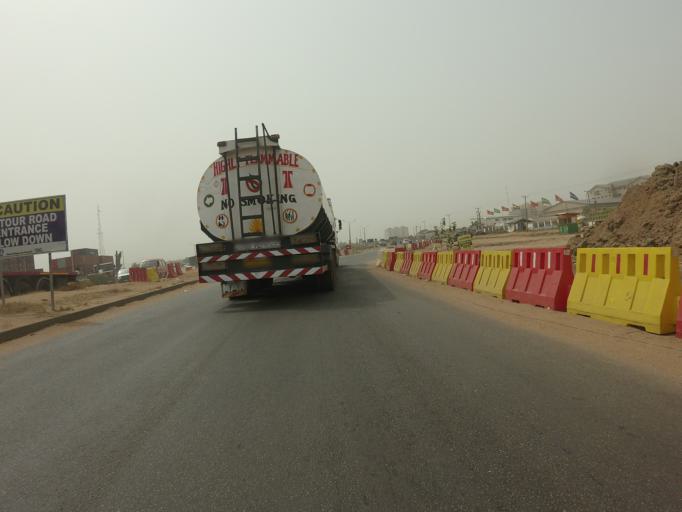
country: GH
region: Greater Accra
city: Tema
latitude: 5.6874
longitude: -0.0116
